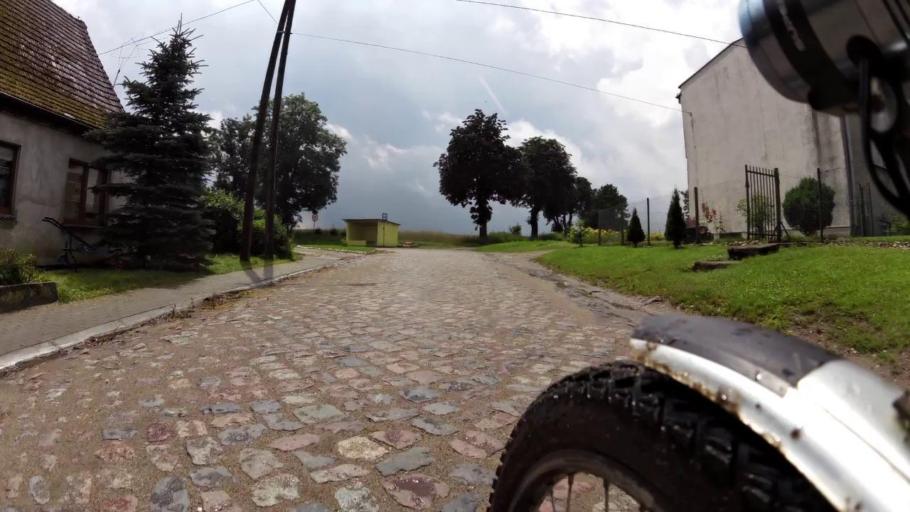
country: PL
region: West Pomeranian Voivodeship
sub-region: Powiat lobeski
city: Lobez
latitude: 53.7325
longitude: 15.6747
